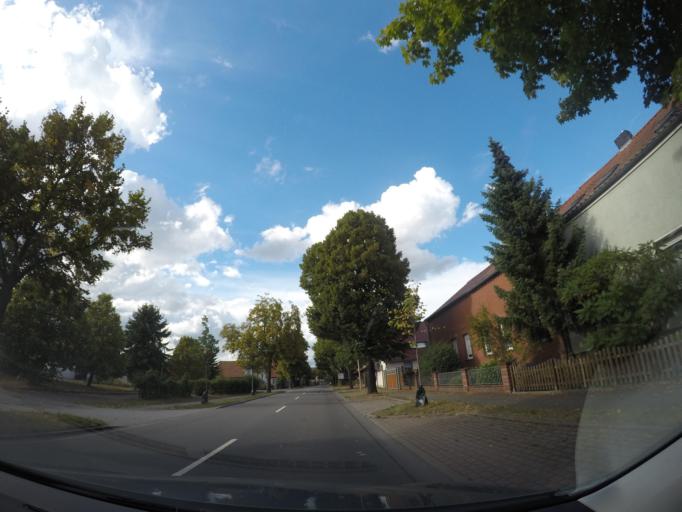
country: DE
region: Saxony-Anhalt
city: Bulstringen
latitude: 52.3181
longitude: 11.3490
